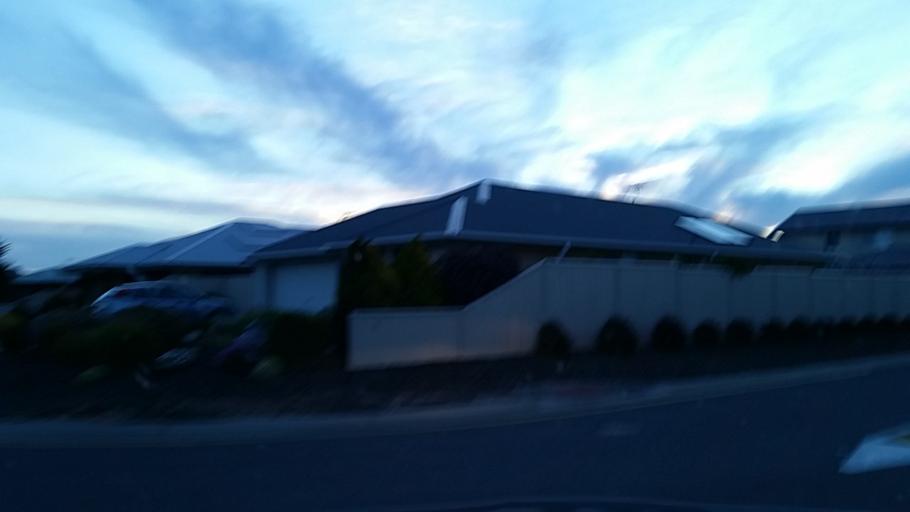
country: AU
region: South Australia
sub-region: Yankalilla
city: Normanville
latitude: -35.4524
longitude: 138.3155
